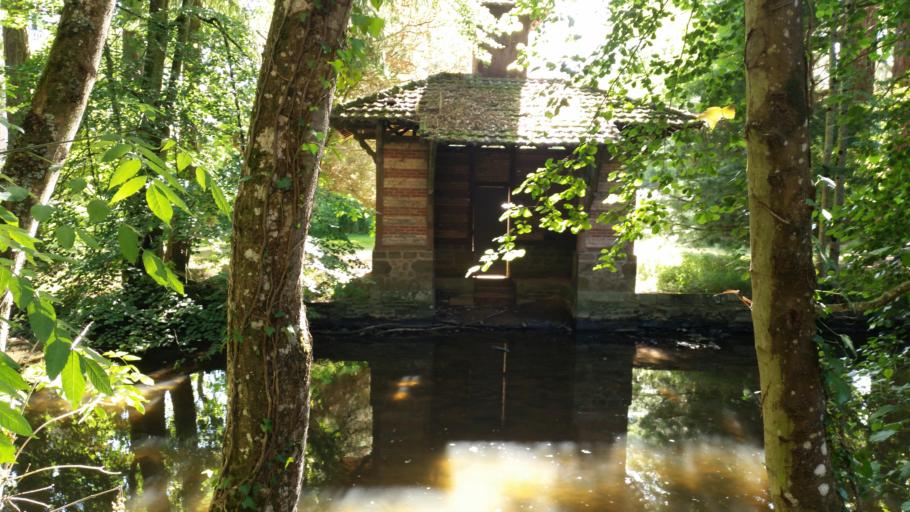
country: FR
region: Lower Normandy
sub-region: Departement du Calvados
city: Clecy
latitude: 48.8408
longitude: -0.3963
